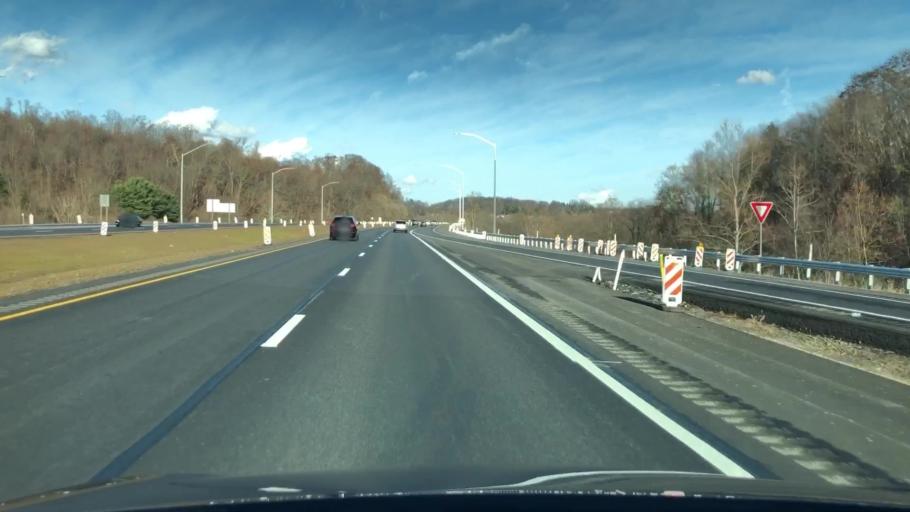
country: US
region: Pennsylvania
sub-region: Allegheny County
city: Brackenridge
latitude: 40.6339
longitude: -79.7292
